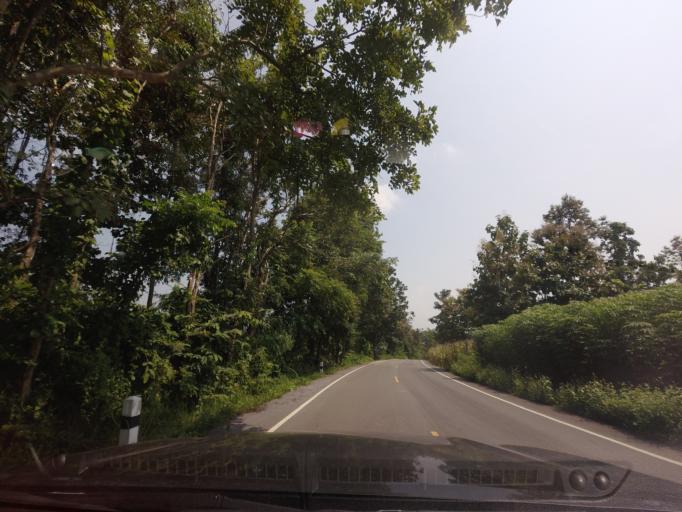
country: TH
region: Nan
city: Nan
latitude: 18.8544
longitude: 100.7870
